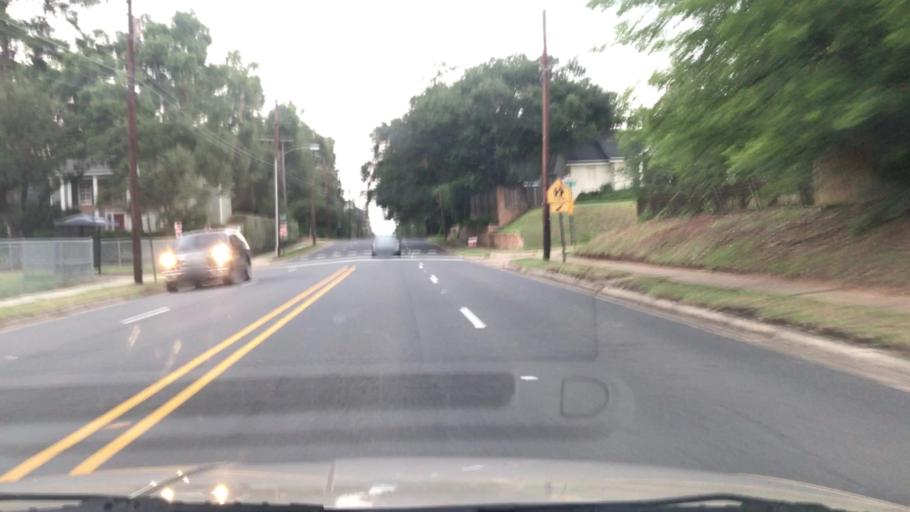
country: US
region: Louisiana
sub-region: Bossier Parish
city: Bossier City
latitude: 32.4602
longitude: -93.7460
